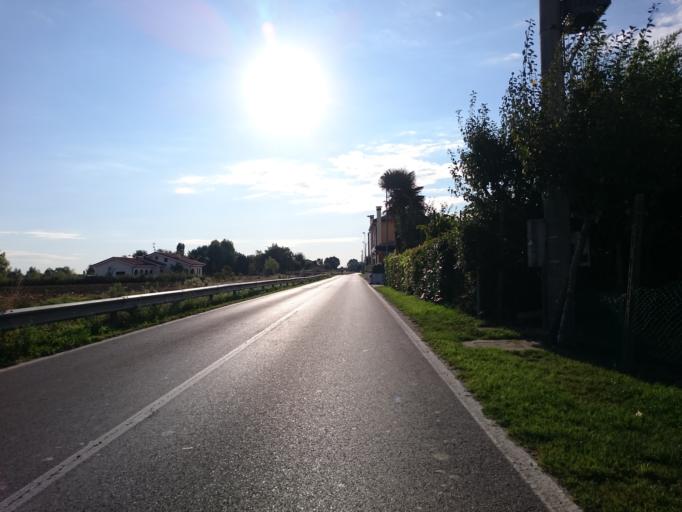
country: IT
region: Veneto
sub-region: Provincia di Padova
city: Terradura
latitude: 45.3286
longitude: 11.8444
